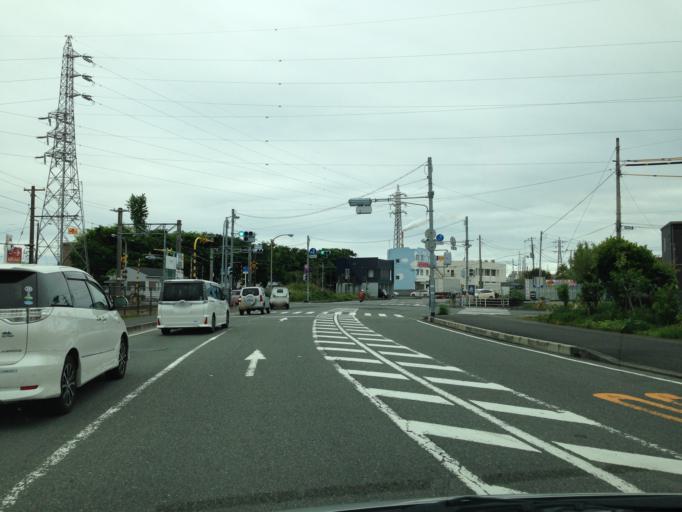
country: JP
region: Shizuoka
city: Fuji
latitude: 35.1554
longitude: 138.6920
